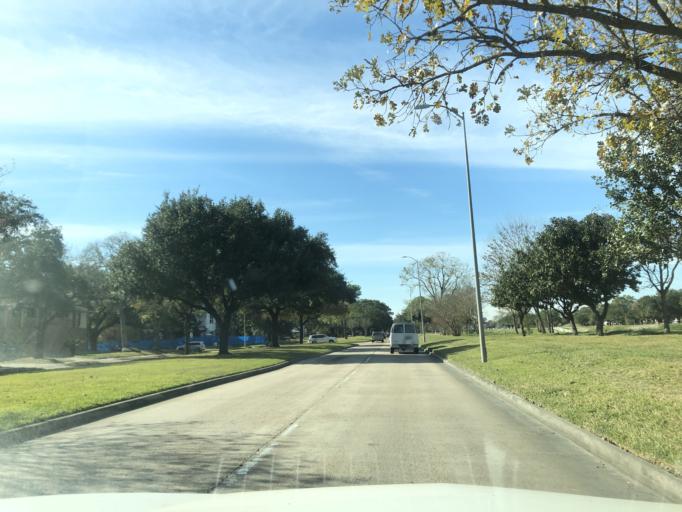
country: US
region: Texas
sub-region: Harris County
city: Bellaire
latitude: 29.6779
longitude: -95.4706
